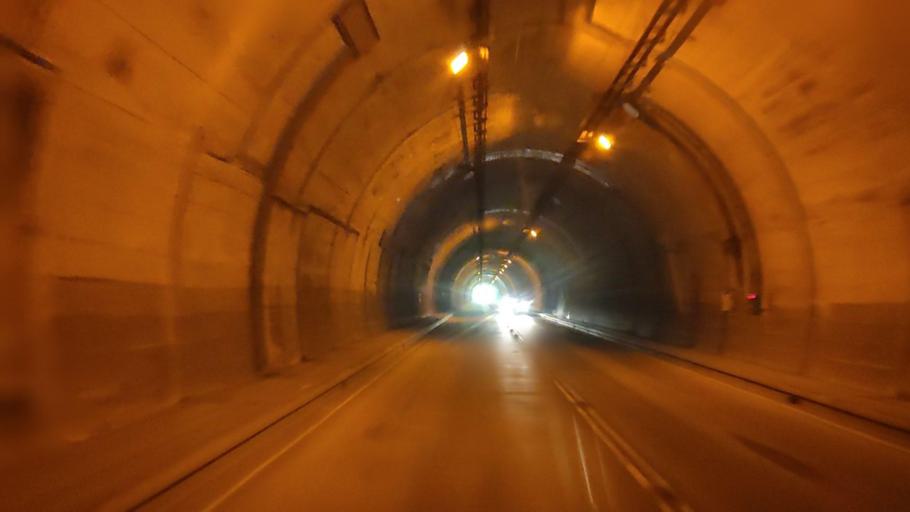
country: JP
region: Shizuoka
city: Ito
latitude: 34.9262
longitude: 139.0437
